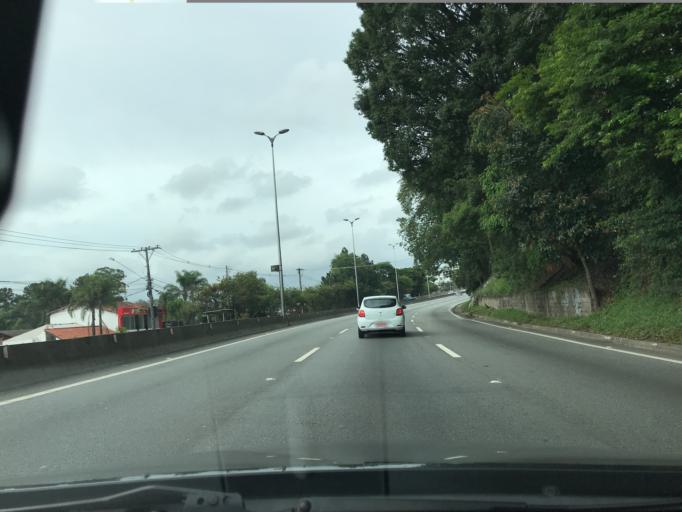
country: BR
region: Sao Paulo
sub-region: Embu
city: Embu
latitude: -23.5962
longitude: -46.8404
